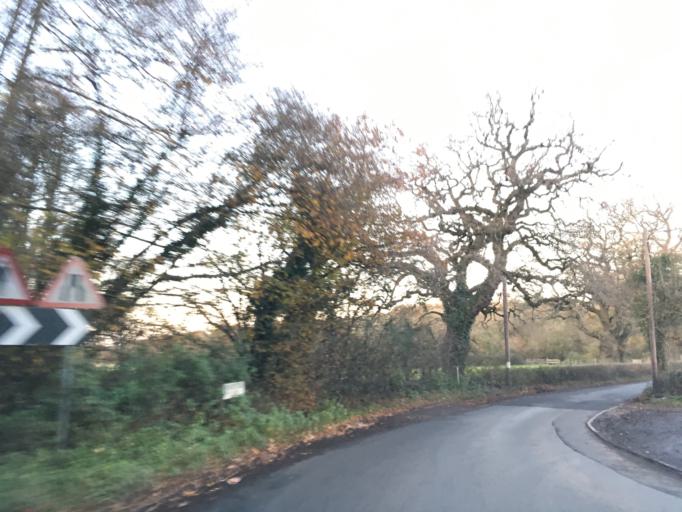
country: GB
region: England
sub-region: Hampshire
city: Bishopstoke
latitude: 50.9827
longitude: -1.3298
